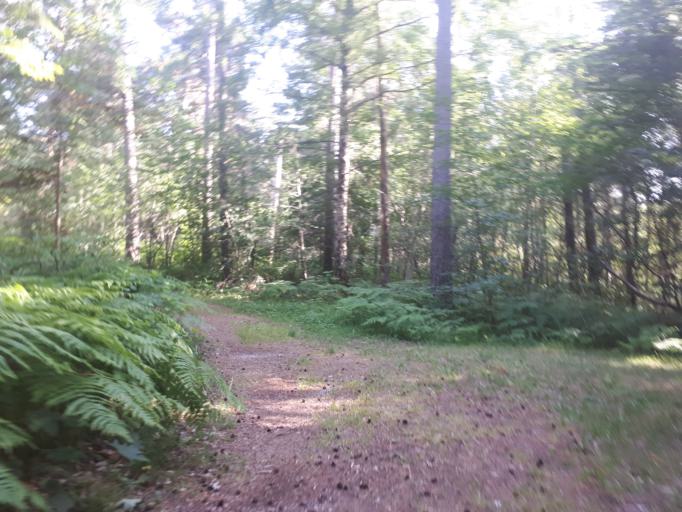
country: SE
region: Gotland
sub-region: Gotland
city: Visby
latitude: 57.6096
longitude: 18.2884
